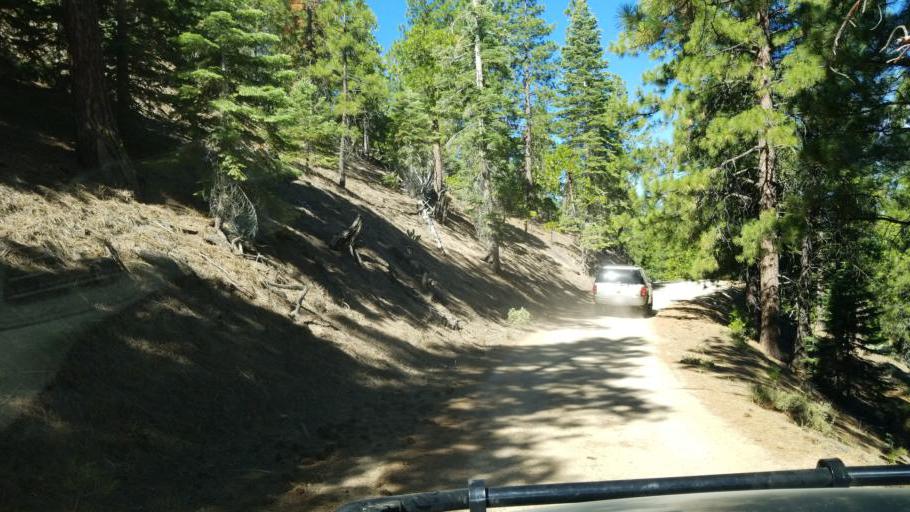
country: US
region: California
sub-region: Lassen County
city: Susanville
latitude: 40.5732
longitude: -120.7497
